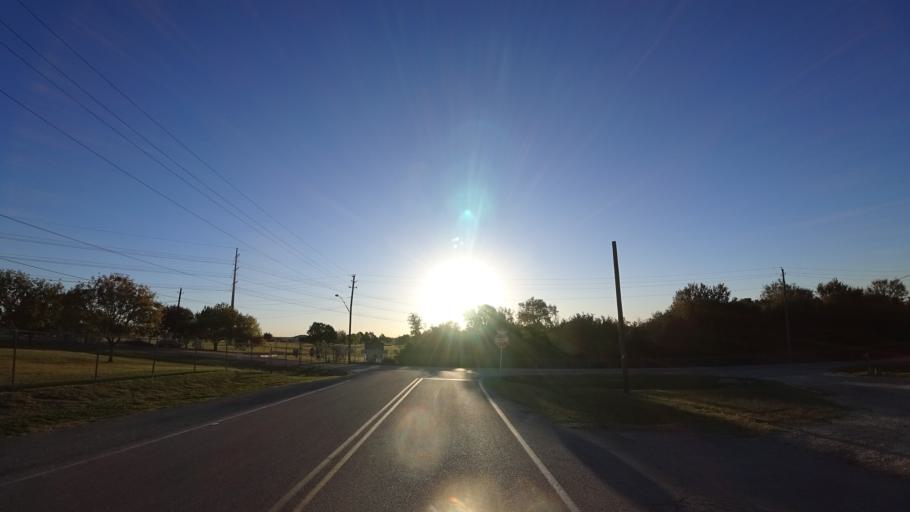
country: US
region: Texas
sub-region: Travis County
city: Hornsby Bend
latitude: 30.2817
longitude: -97.6096
